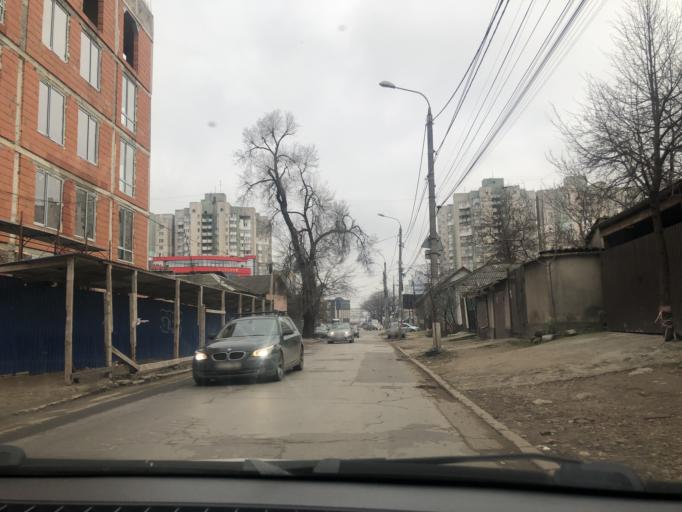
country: MD
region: Chisinau
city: Chisinau
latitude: 47.0204
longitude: 28.8498
